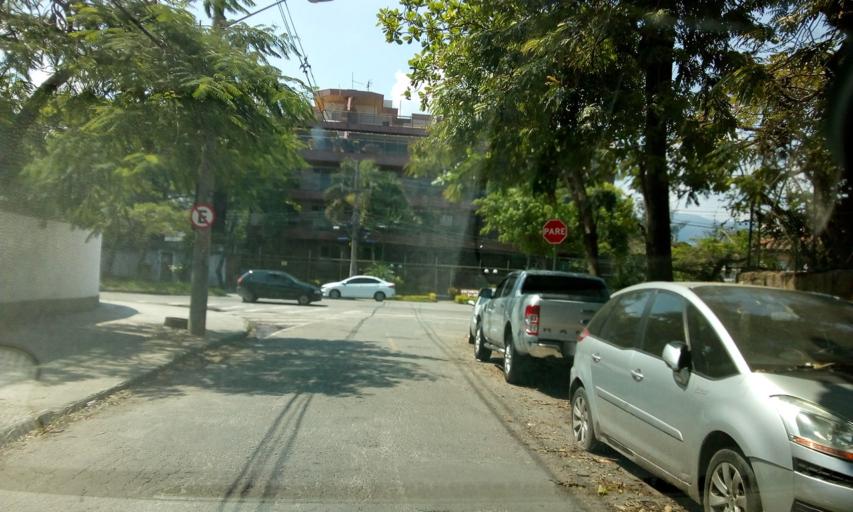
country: BR
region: Rio de Janeiro
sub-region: Nilopolis
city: Nilopolis
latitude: -23.0219
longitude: -43.4778
